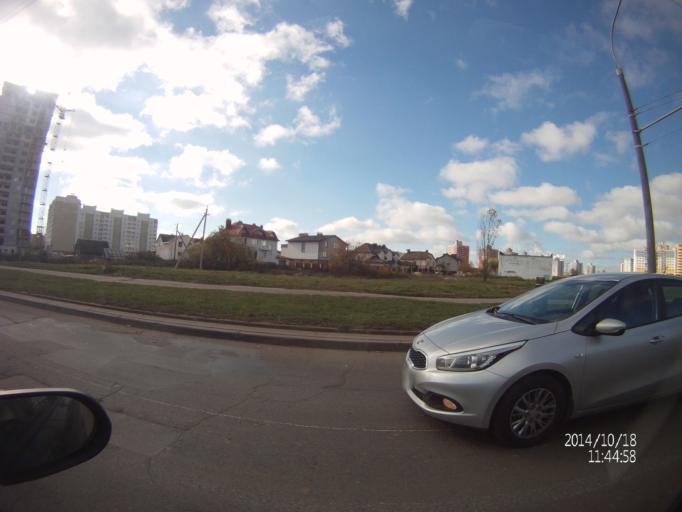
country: BY
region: Minsk
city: Novoye Medvezhino
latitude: 53.8775
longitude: 27.4601
